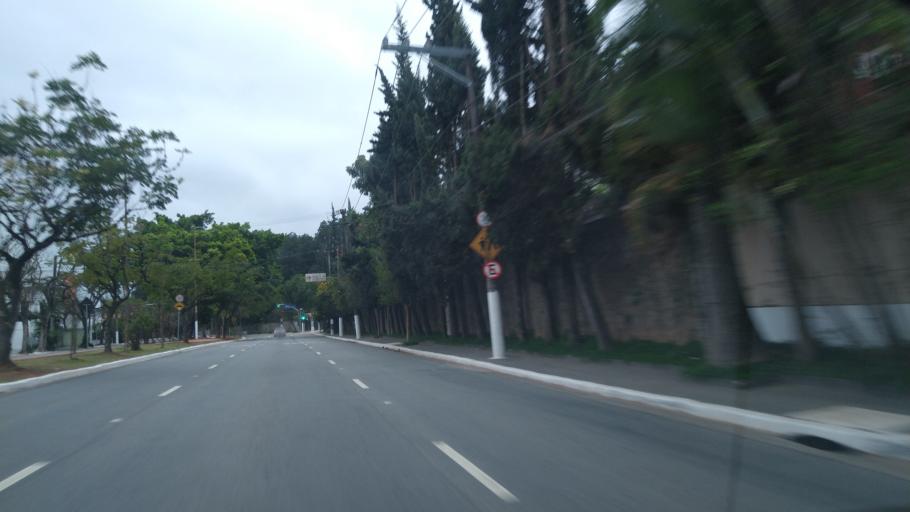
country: BR
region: Sao Paulo
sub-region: Taboao Da Serra
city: Taboao da Serra
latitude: -23.5958
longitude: -46.7202
